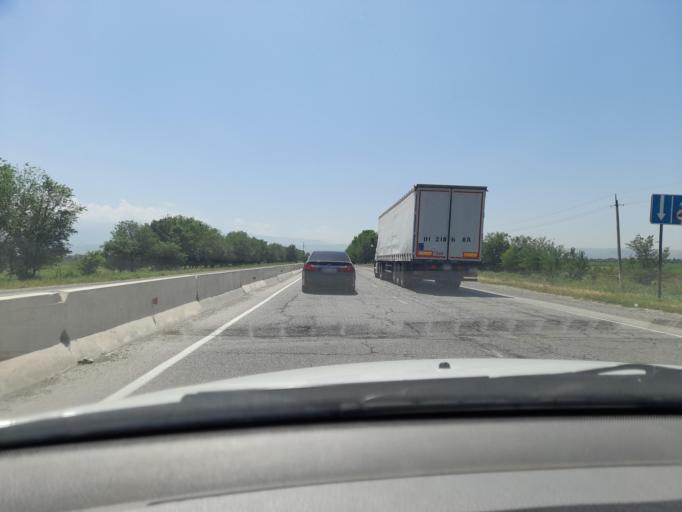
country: UZ
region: Jizzax
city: Jizzax
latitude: 40.1143
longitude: 67.9450
